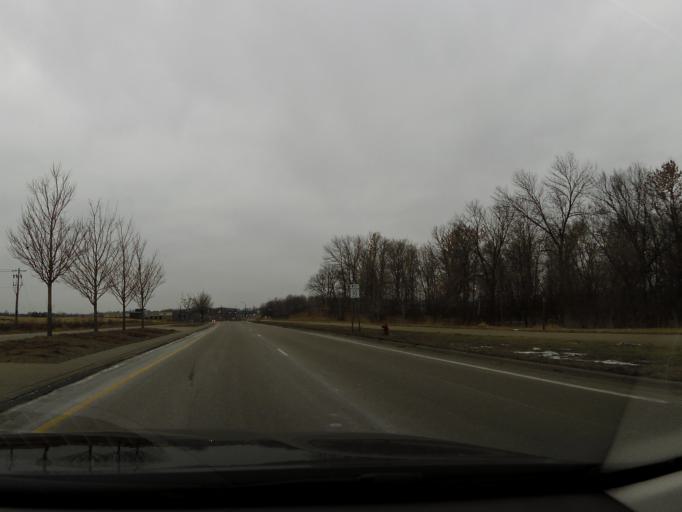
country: US
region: Minnesota
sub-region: Carver County
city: Chaska
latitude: 44.8059
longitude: -93.6269
